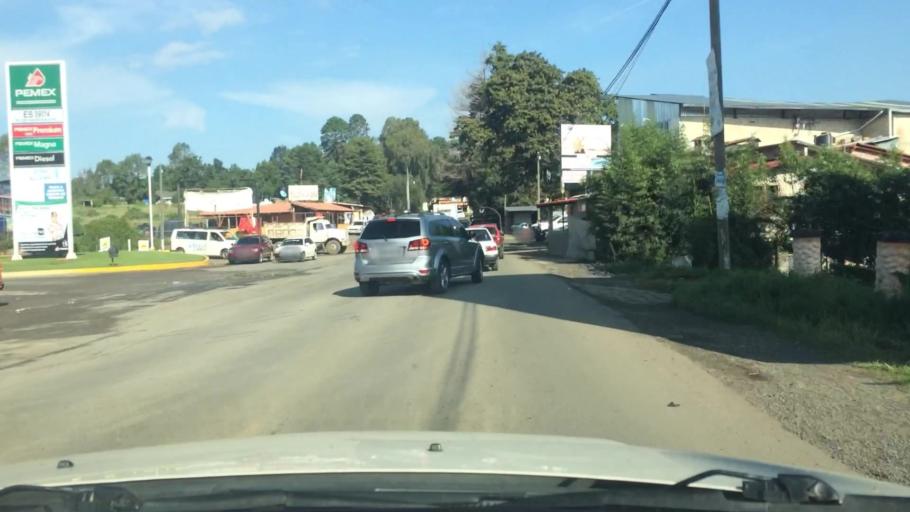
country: MX
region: Mexico
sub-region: Valle de Bravo
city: Cuadrilla de Dolores
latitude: 19.1473
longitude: -100.0703
